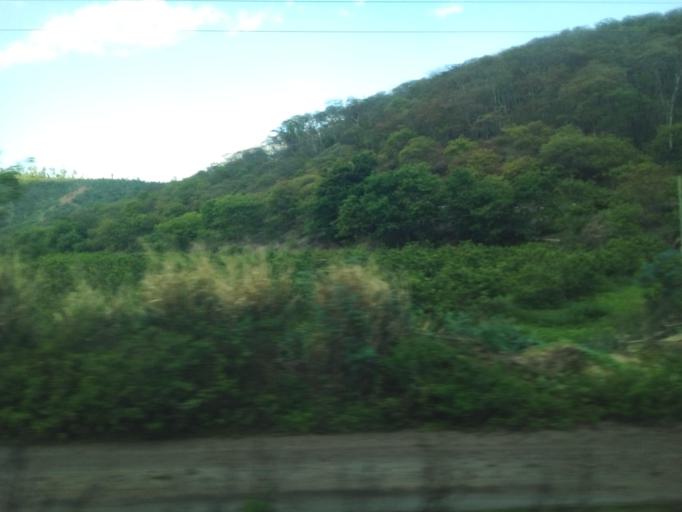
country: BR
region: Minas Gerais
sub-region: Conselheiro Pena
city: Conselheiro Pena
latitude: -19.1386
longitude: -41.4813
